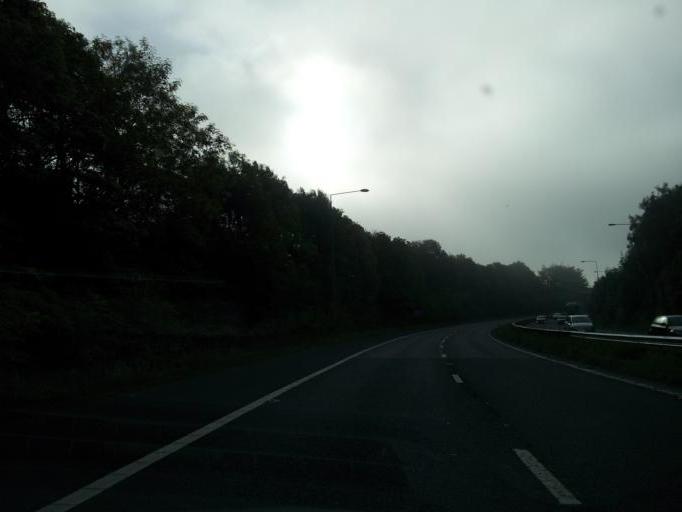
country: GB
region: England
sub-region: Borough of Oldham
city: Royton
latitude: 53.5591
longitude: -2.1419
